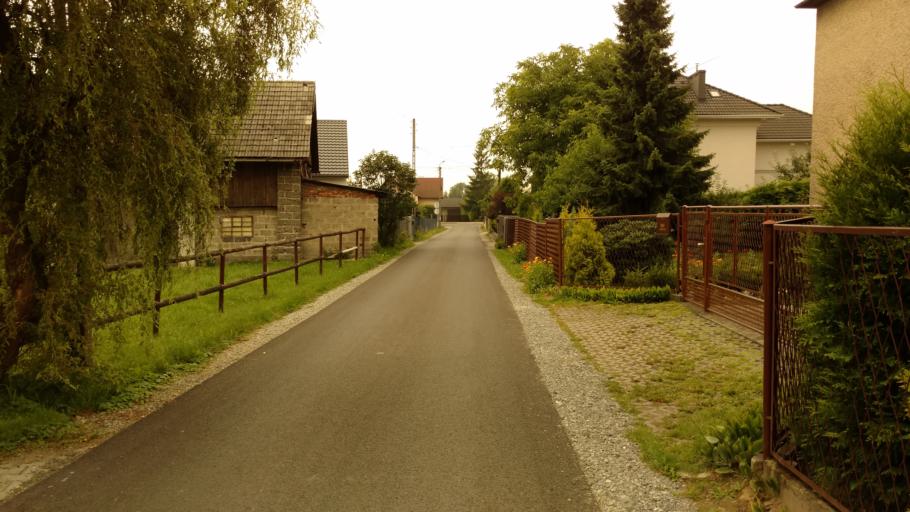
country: PL
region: Silesian Voivodeship
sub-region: Powiat pszczynski
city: Pszczyna
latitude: 49.9949
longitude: 18.9657
